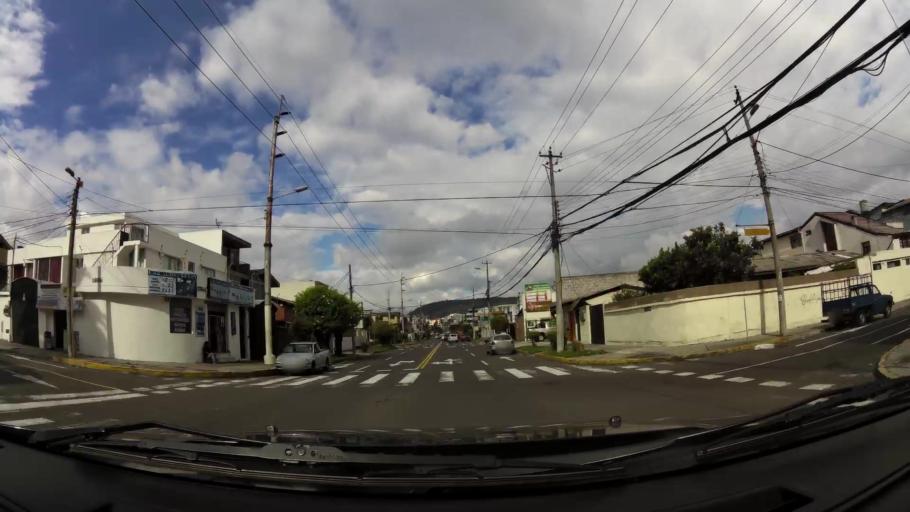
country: EC
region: Pichincha
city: Quito
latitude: -0.1616
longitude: -78.4850
